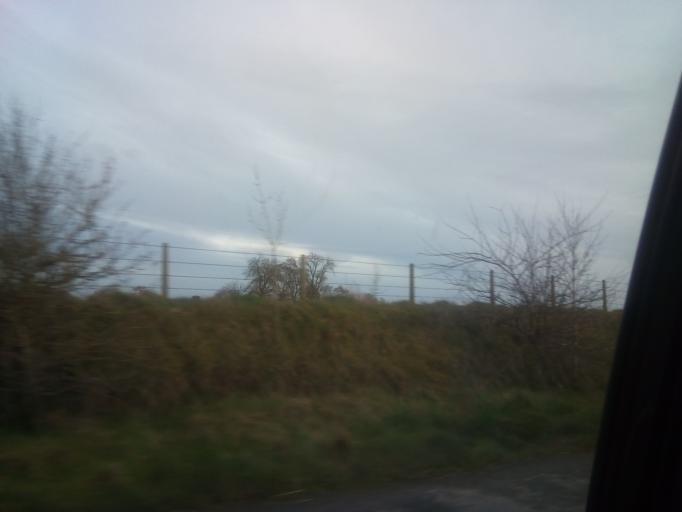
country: IE
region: Leinster
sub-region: Laois
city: Abbeyleix
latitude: 52.8535
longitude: -7.3877
